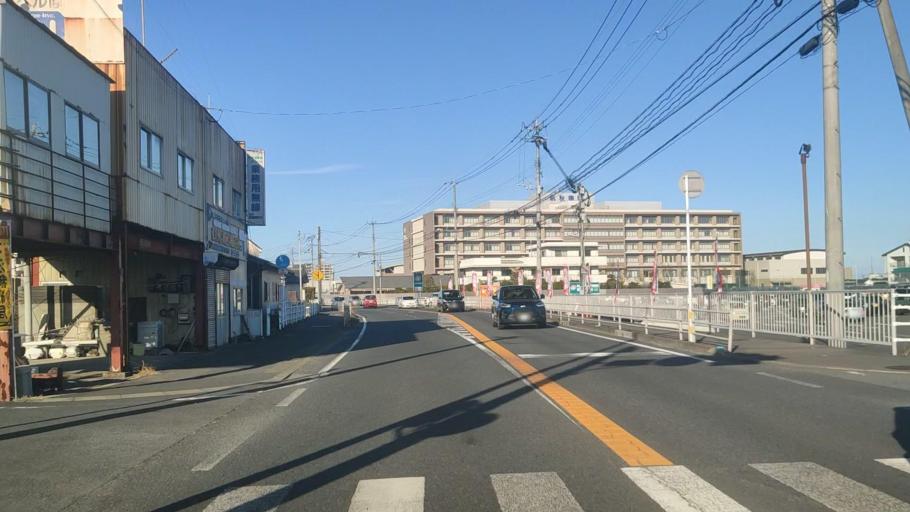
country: JP
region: Oita
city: Oita
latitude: 33.2227
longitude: 131.6184
